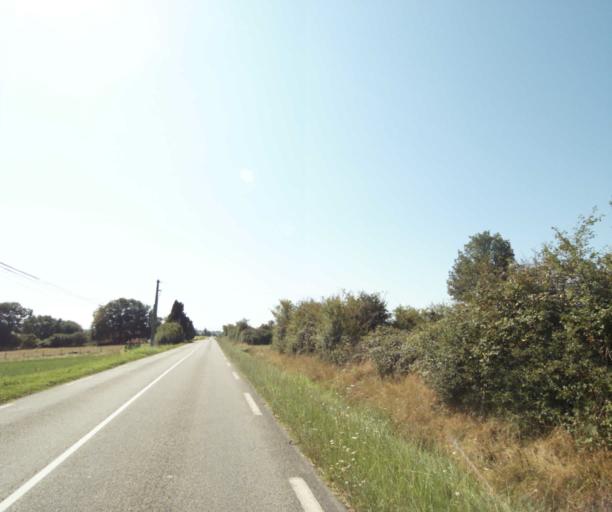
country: FR
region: Midi-Pyrenees
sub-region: Departement de l'Ariege
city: Lezat-sur-Leze
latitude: 43.2971
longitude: 1.3382
